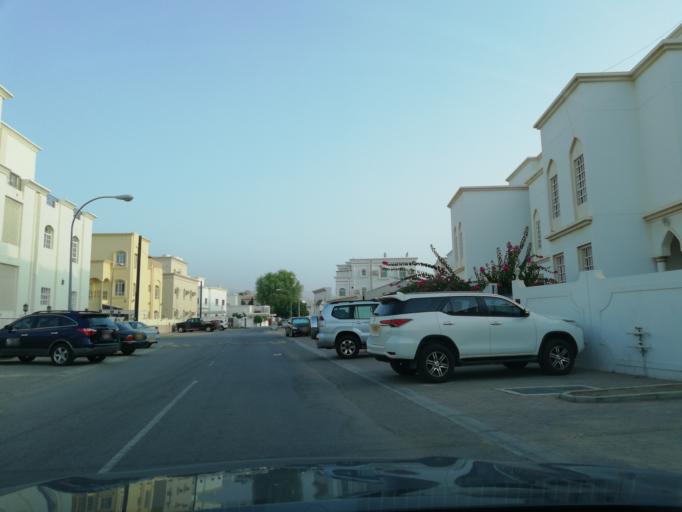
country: OM
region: Muhafazat Masqat
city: Bawshar
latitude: 23.5986
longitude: 58.3890
